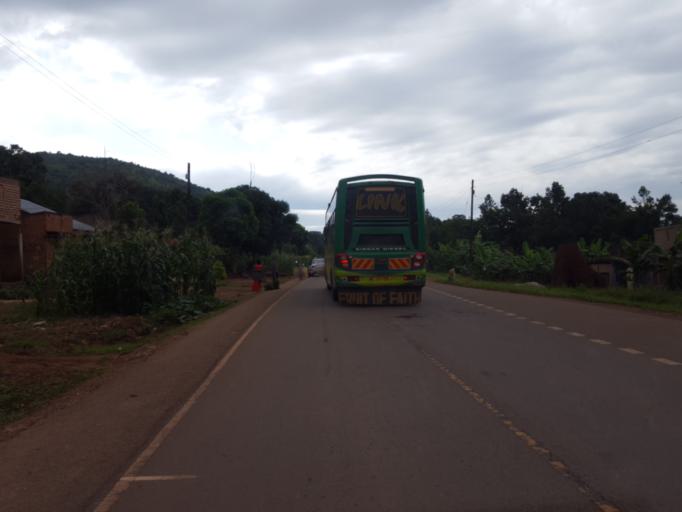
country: UG
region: Central Region
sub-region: Mityana District
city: Mityana
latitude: 0.6716
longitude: 32.0778
